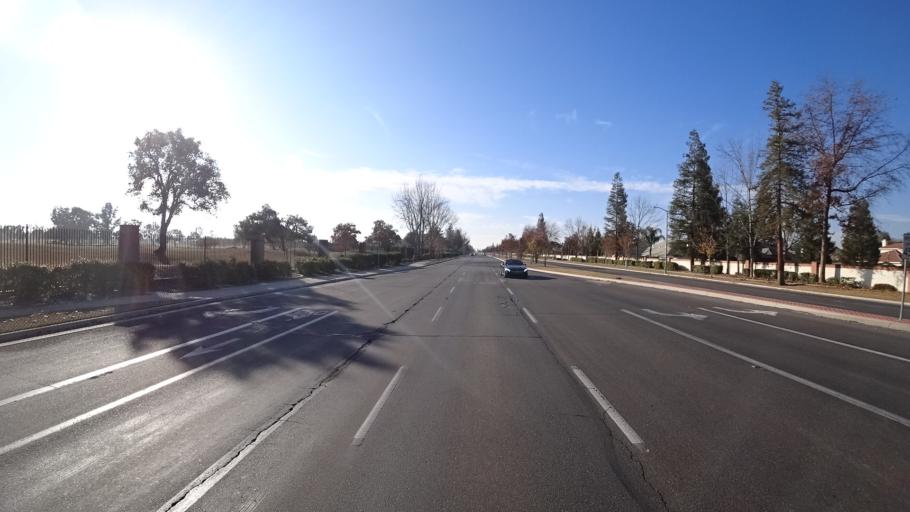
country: US
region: California
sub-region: Kern County
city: Greenacres
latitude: 35.3397
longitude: -119.1151
